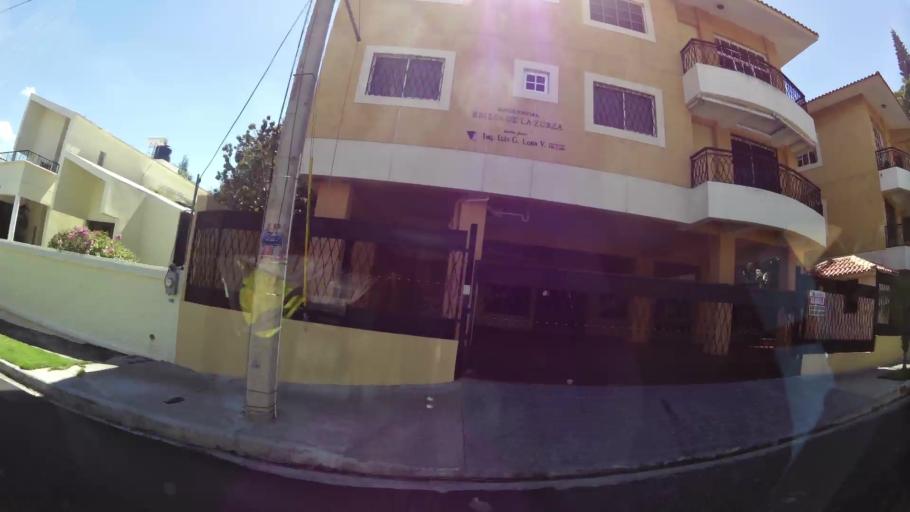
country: DO
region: Santiago
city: Santiago de los Caballeros
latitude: 19.4486
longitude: -70.6925
